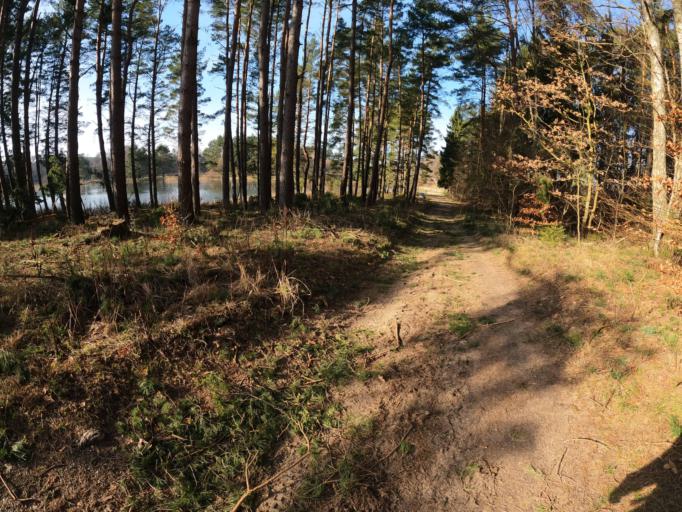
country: PL
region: West Pomeranian Voivodeship
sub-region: Powiat koszalinski
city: Polanow
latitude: 54.1123
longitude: 16.6956
